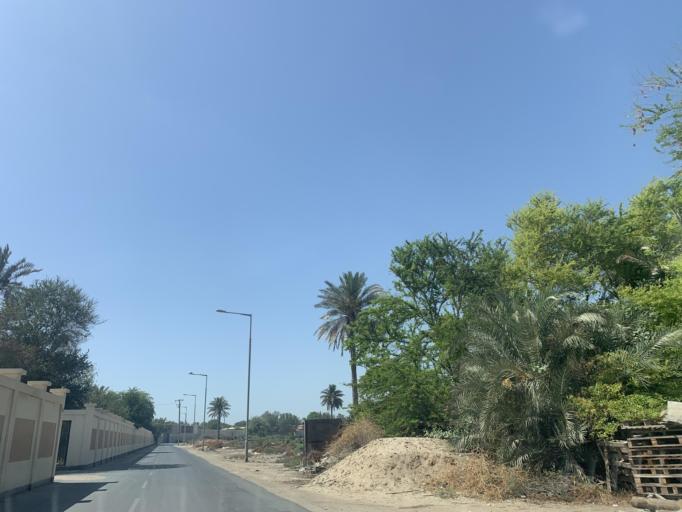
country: BH
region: Manama
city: Jidd Hafs
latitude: 26.2268
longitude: 50.4987
